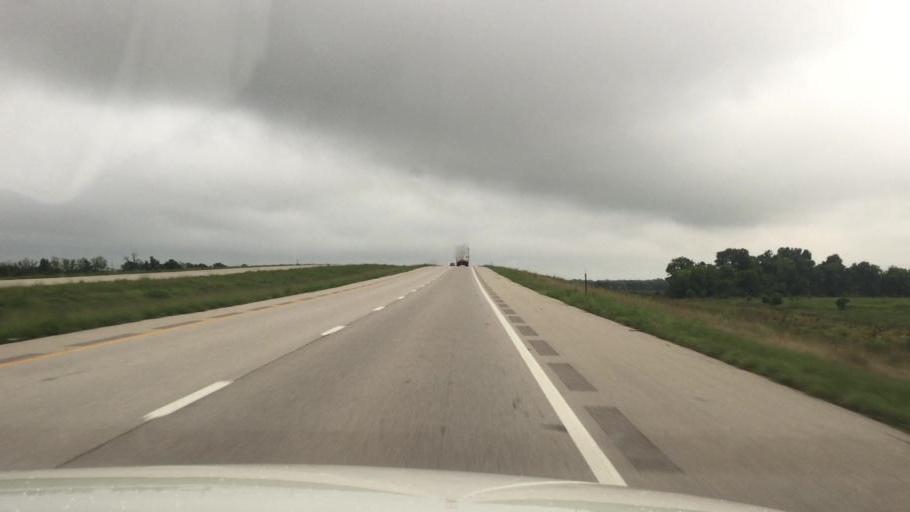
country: US
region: Kansas
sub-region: Montgomery County
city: Coffeyville
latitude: 37.0899
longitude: -95.5898
